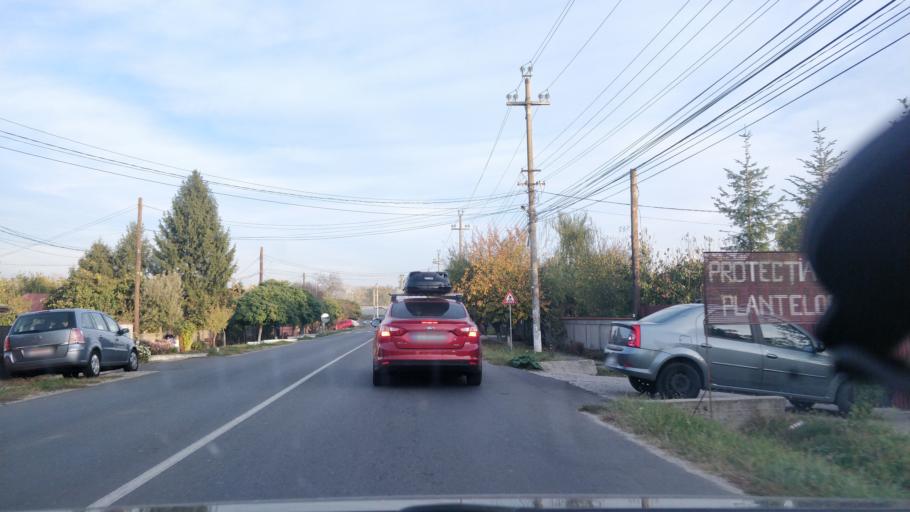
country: RO
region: Ilfov
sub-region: Comuna Ciorogarla
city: Ciorogarla
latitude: 44.4433
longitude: 25.8726
